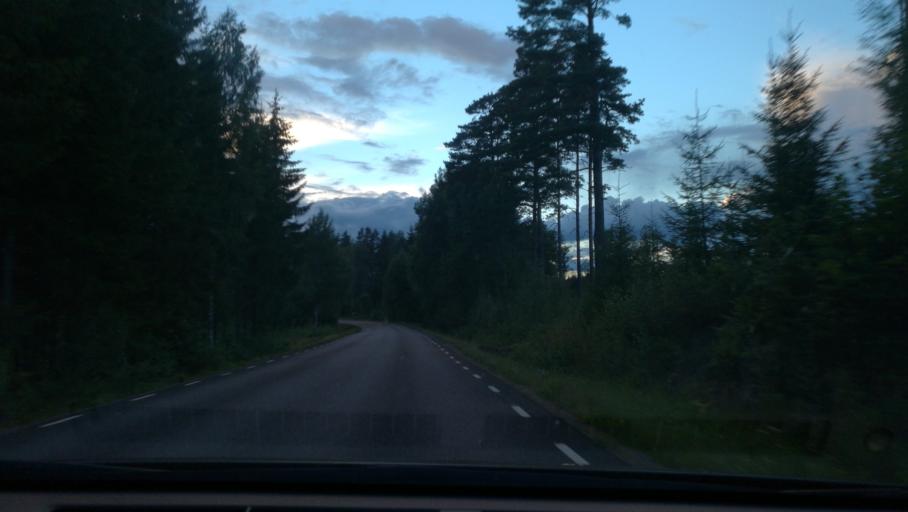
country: SE
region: OEstergoetland
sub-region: Norrkopings Kommun
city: Svartinge
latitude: 58.8213
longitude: 15.9987
